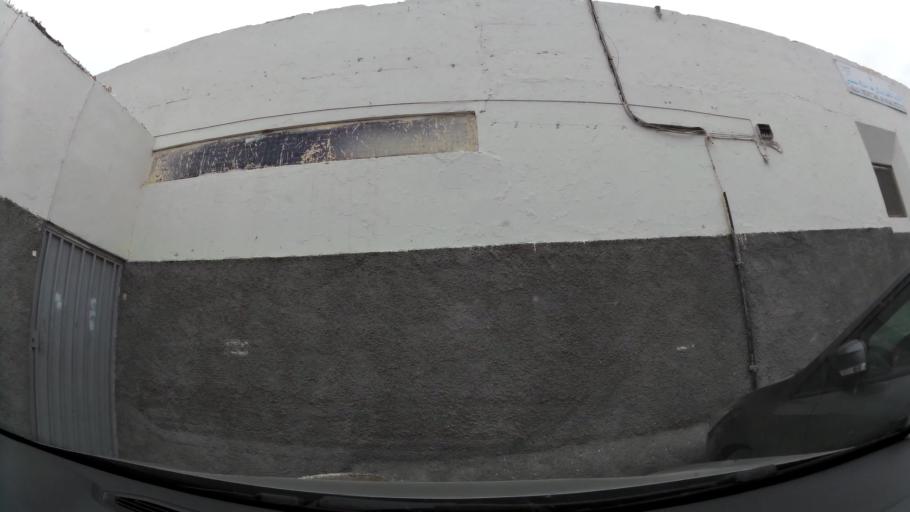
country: MA
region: Fes-Boulemane
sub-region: Fes
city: Fes
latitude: 34.0568
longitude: -4.9747
